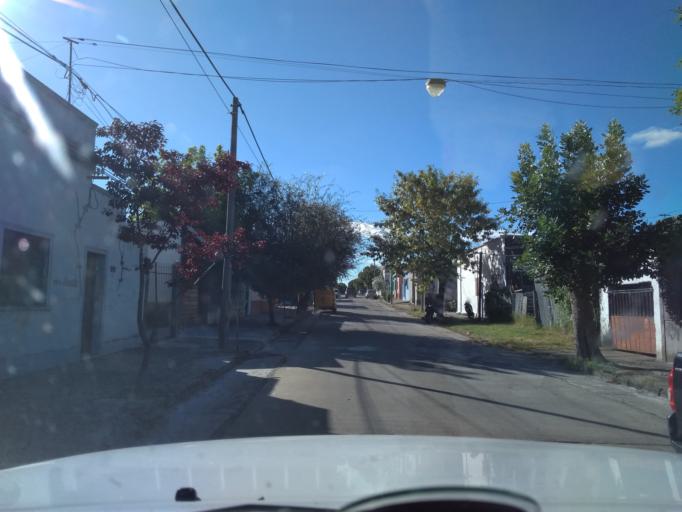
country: UY
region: Florida
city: Florida
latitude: -34.0931
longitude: -56.2129
